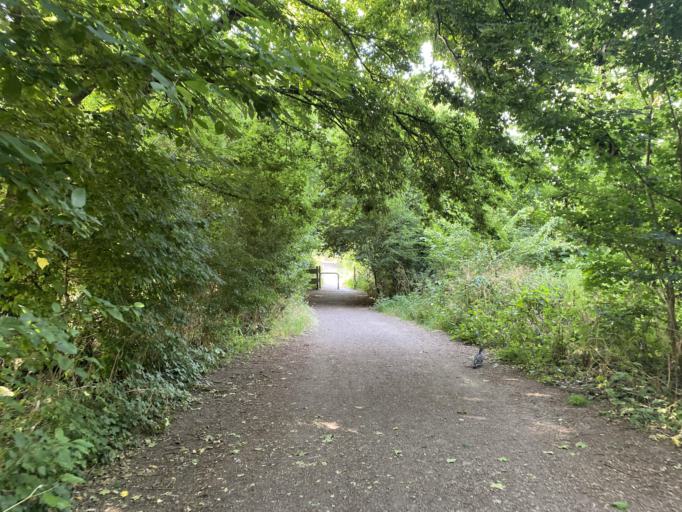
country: GB
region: England
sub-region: Suffolk
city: Haverhill
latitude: 52.0805
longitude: 0.4482
